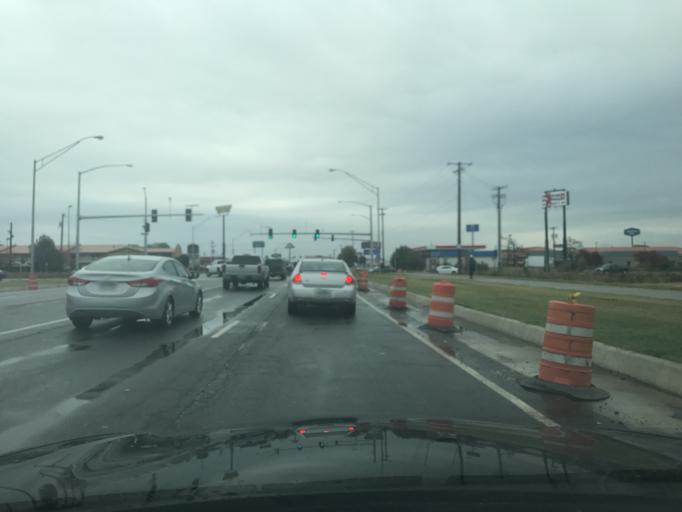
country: US
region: Arkansas
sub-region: Faulkner County
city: Conway
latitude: 35.0915
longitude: -92.4221
